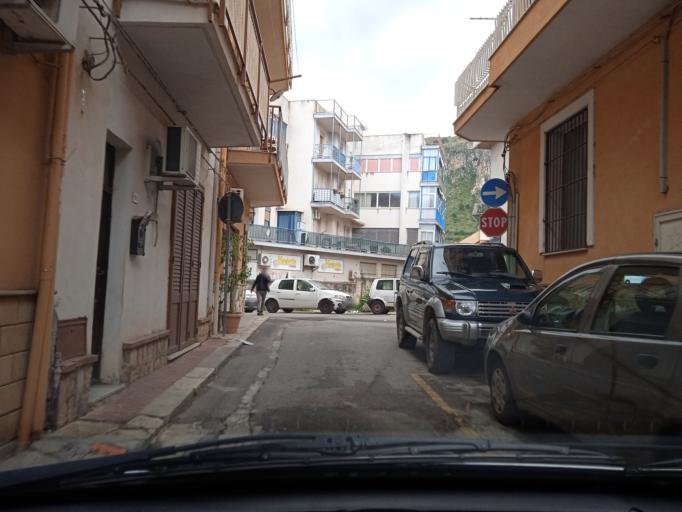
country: IT
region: Sicily
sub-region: Palermo
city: Villabate
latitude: 38.0754
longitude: 13.4410
